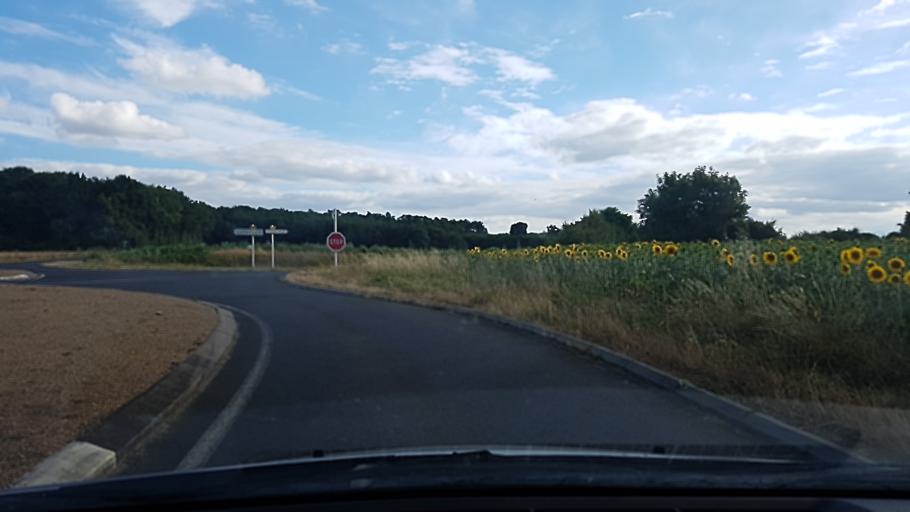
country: FR
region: Pays de la Loire
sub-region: Departement de Maine-et-Loire
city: Jarze
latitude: 47.5096
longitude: -0.2182
